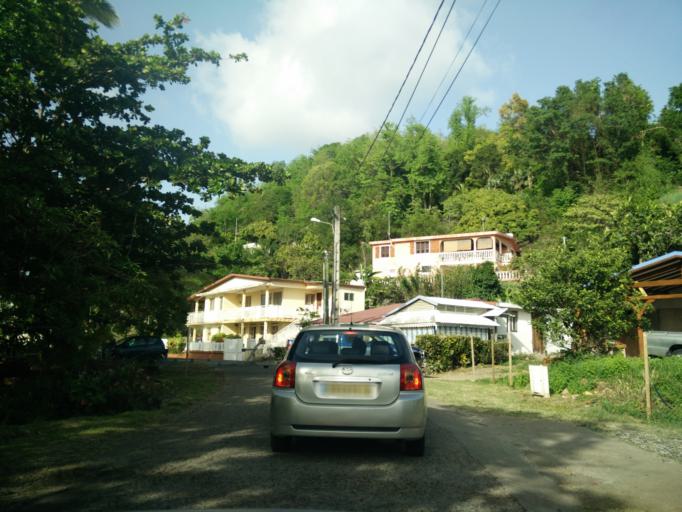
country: MQ
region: Martinique
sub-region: Martinique
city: Riviere-Pilote
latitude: 14.4657
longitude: -60.9109
